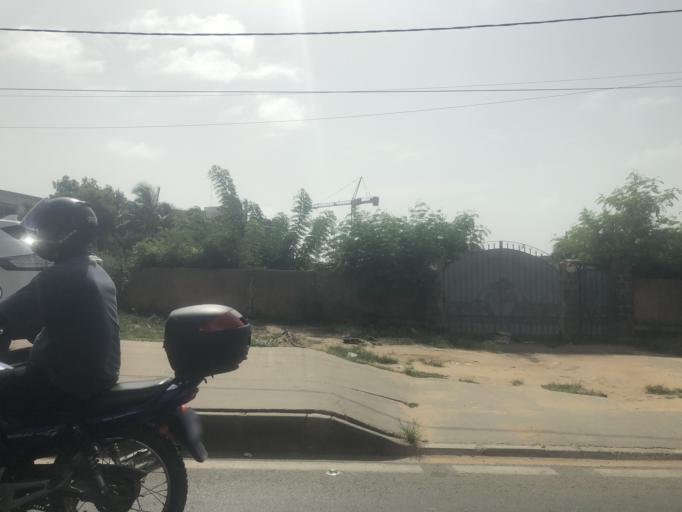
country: SN
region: Dakar
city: Mermoz Boabab
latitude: 14.7402
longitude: -17.5104
